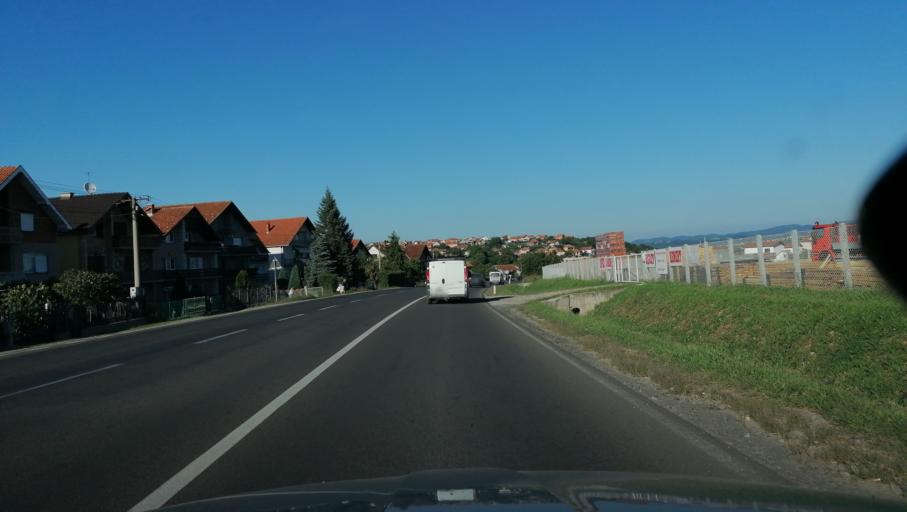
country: RS
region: Central Serbia
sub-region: Sumadijski Okrug
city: Kragujevac
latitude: 43.9914
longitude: 20.8590
